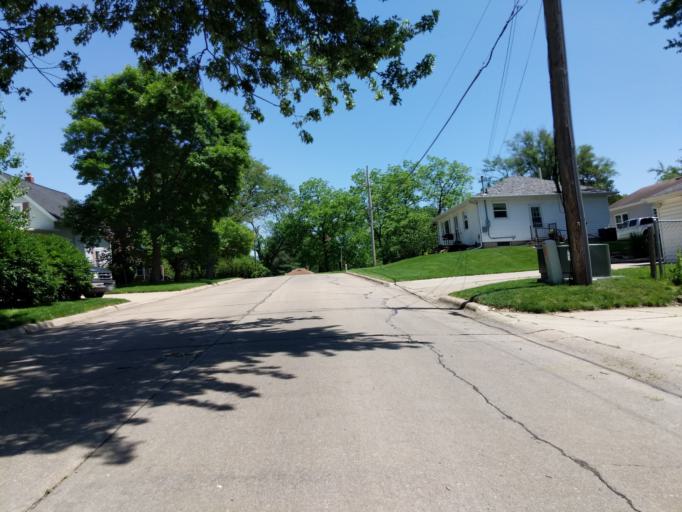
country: US
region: Iowa
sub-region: Linn County
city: Cedar Rapids
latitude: 42.0185
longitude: -91.6383
